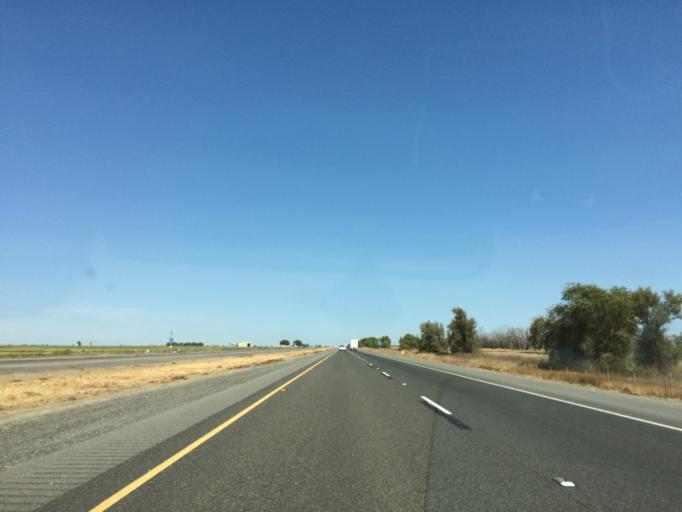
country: US
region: California
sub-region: Glenn County
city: Willows
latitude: 39.4274
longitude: -122.1932
